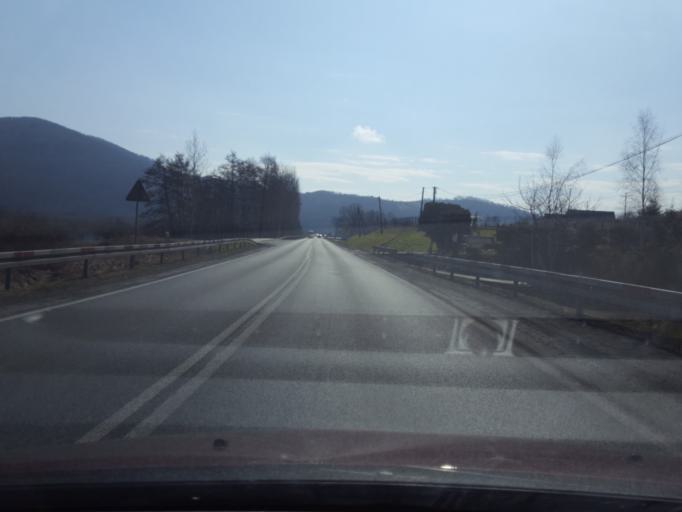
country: PL
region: Lesser Poland Voivodeship
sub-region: Powiat nowosadecki
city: Lososina Dolna
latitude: 49.7024
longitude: 20.6549
